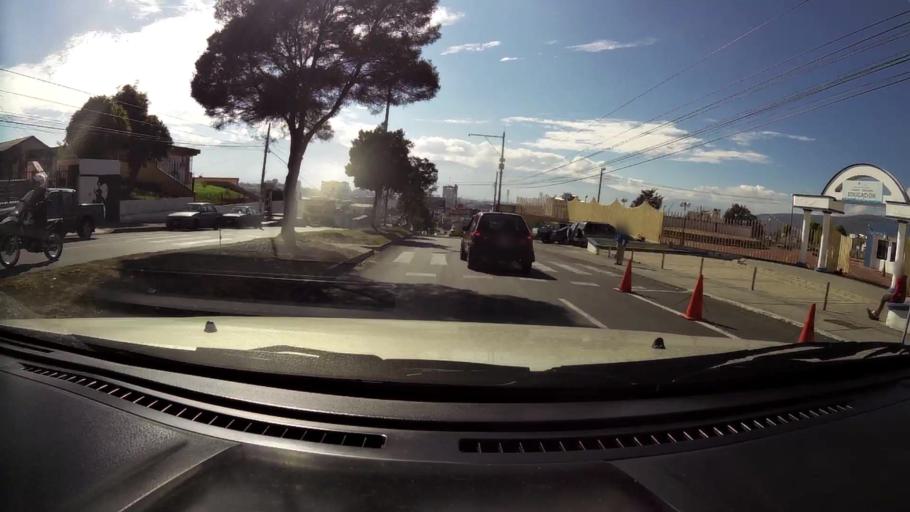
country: EC
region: Chimborazo
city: Riobamba
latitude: -1.6602
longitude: -78.6650
